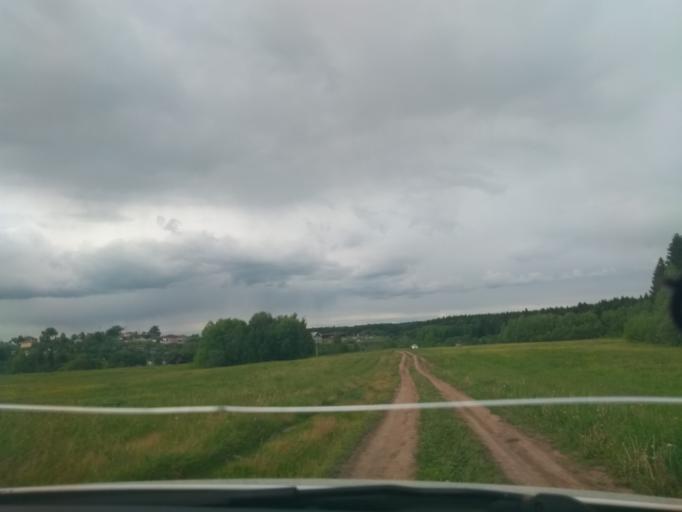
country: RU
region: Perm
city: Perm
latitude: 57.9868
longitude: 56.3338
